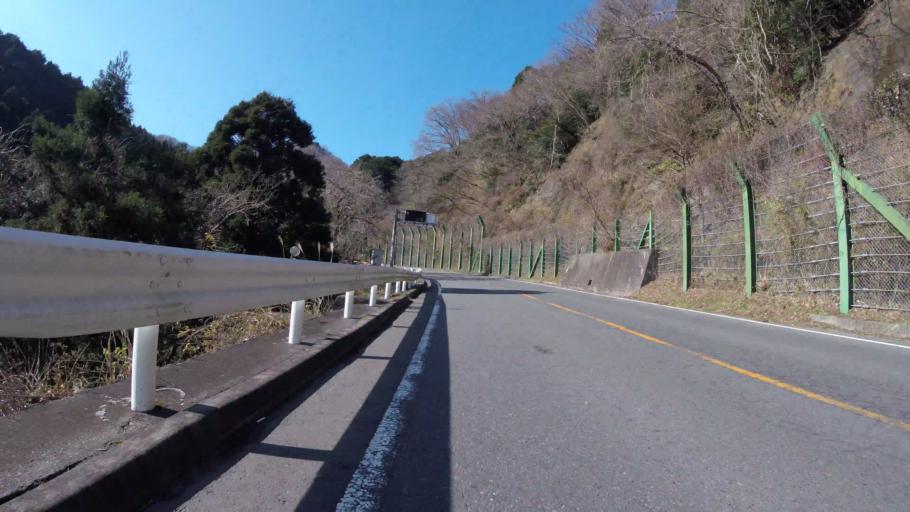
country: JP
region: Shizuoka
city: Ito
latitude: 34.9299
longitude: 139.0490
